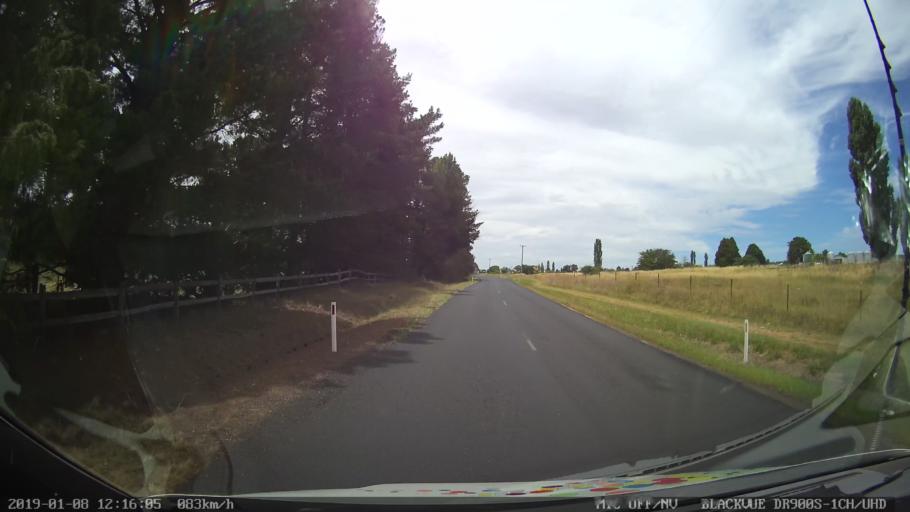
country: AU
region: New South Wales
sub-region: Armidale Dumaresq
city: Armidale
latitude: -30.4956
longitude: 151.6326
